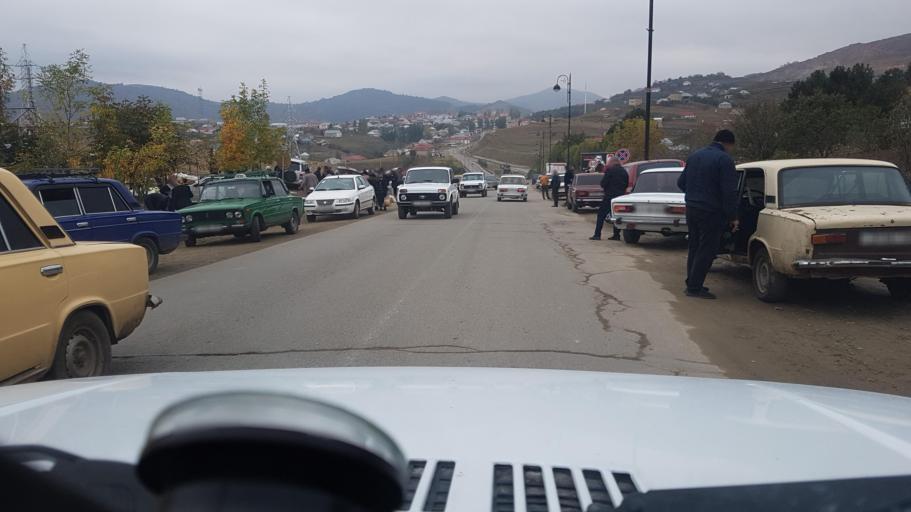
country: AZ
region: Gadabay Rayon
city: Ariqdam
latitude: 40.5906
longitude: 45.8115
